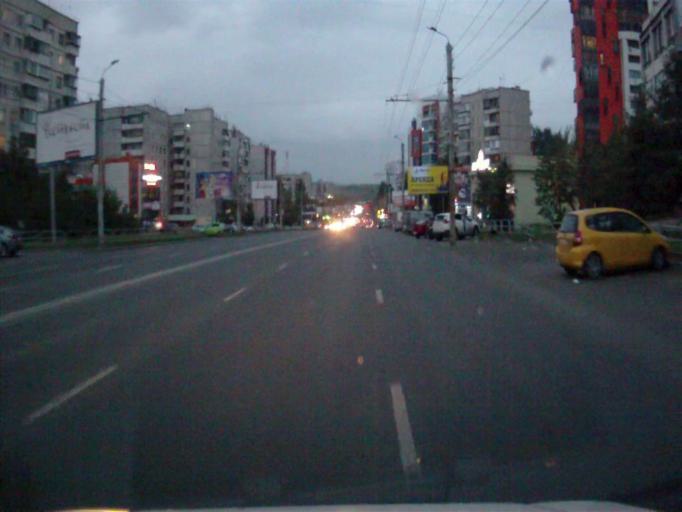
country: RU
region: Chelyabinsk
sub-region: Gorod Chelyabinsk
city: Chelyabinsk
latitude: 55.1863
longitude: 61.3325
